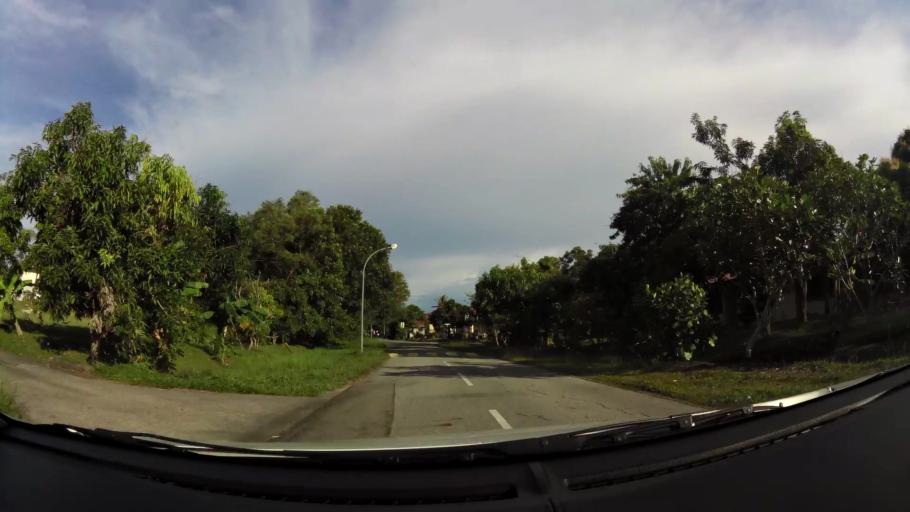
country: BN
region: Brunei and Muara
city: Bandar Seri Begawan
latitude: 4.9837
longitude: 114.9672
